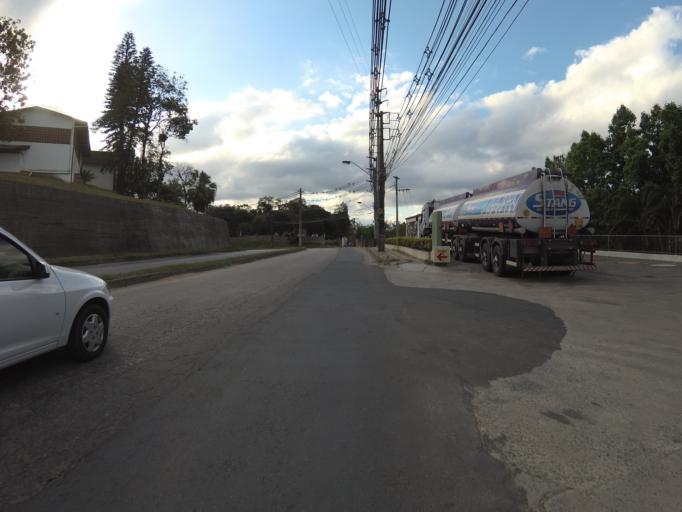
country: BR
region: Santa Catarina
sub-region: Blumenau
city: Blumenau
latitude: -26.8818
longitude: -49.1028
